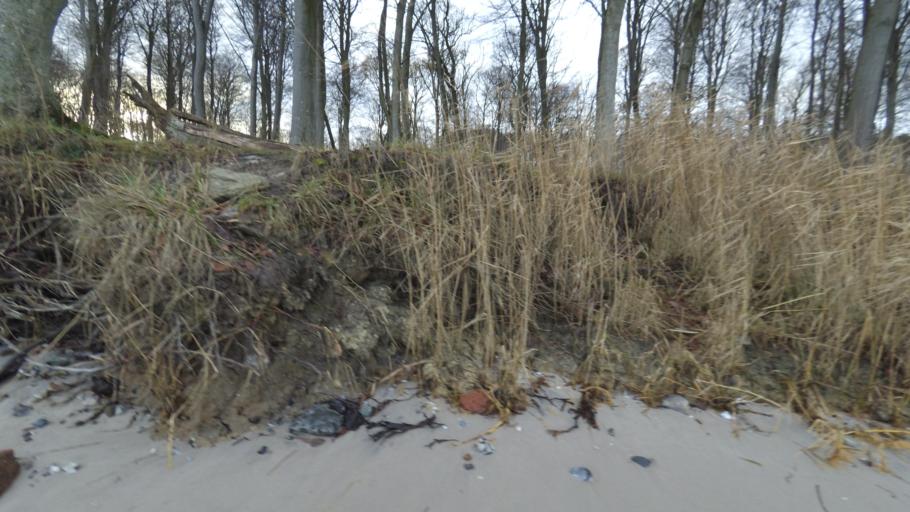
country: DK
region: Central Jutland
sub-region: Arhus Kommune
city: Beder
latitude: 56.0720
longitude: 10.2552
